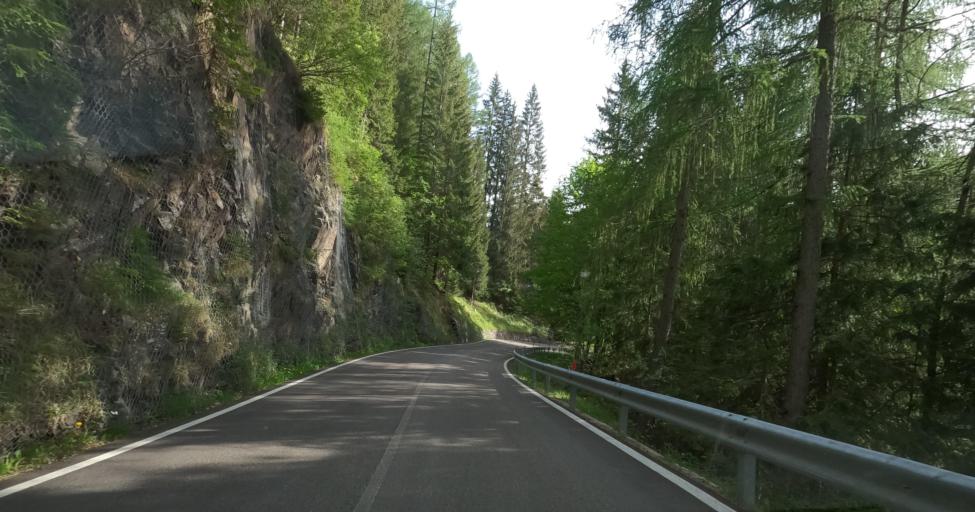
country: IT
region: Veneto
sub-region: Provincia di Belluno
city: Colle Santa Lucia
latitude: 46.4575
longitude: 11.9905
